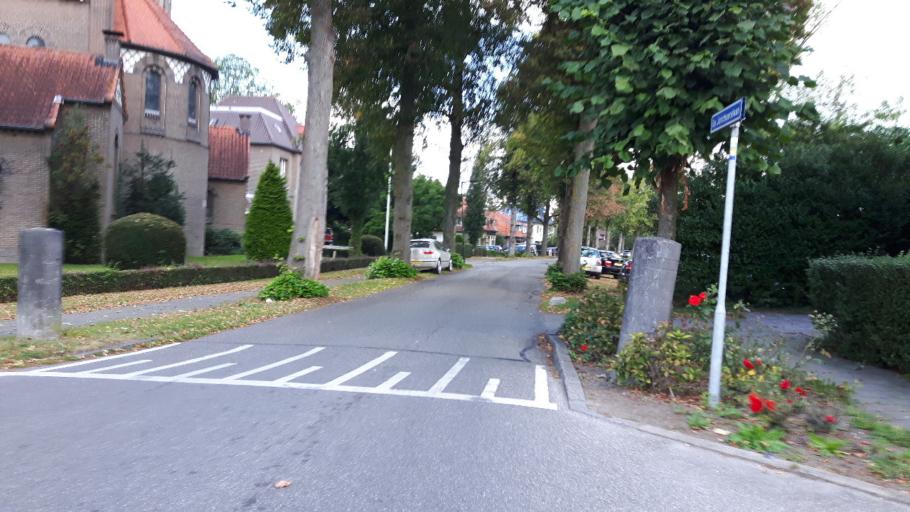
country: NL
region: Utrecht
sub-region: Gemeente Montfoort
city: Montfoort
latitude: 52.0922
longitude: 4.9628
